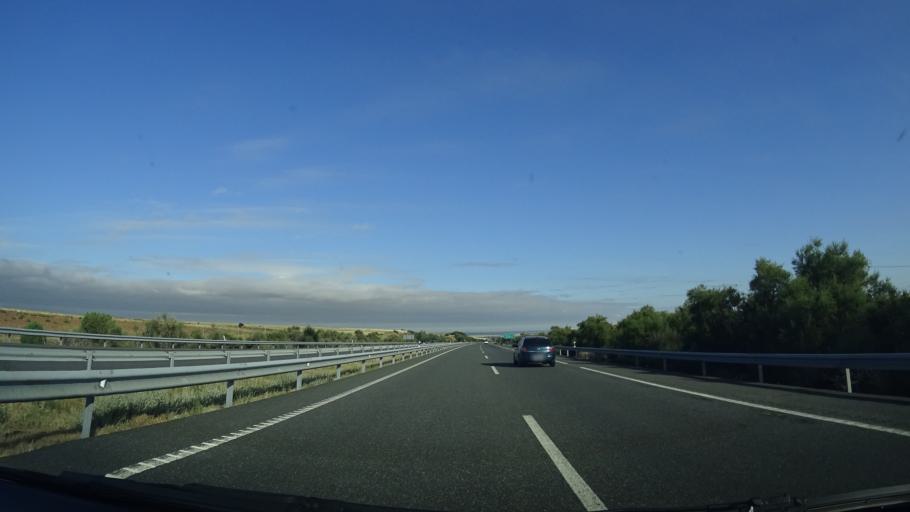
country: ES
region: Castille and Leon
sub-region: Provincia de Avila
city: Maello
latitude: 40.8259
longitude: -4.5169
